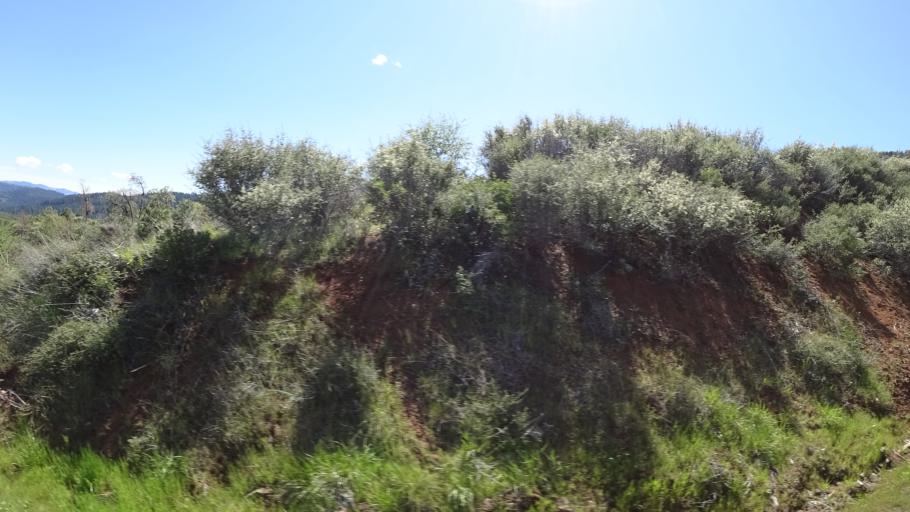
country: US
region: California
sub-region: Trinity County
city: Weaverville
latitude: 40.7464
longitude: -122.9720
